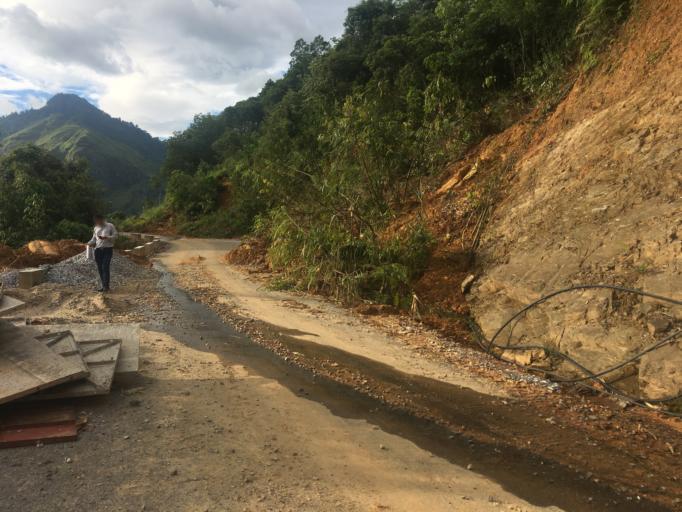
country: VN
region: Ha Giang
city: Thi Tran Tam Son
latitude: 22.9481
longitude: 105.0257
